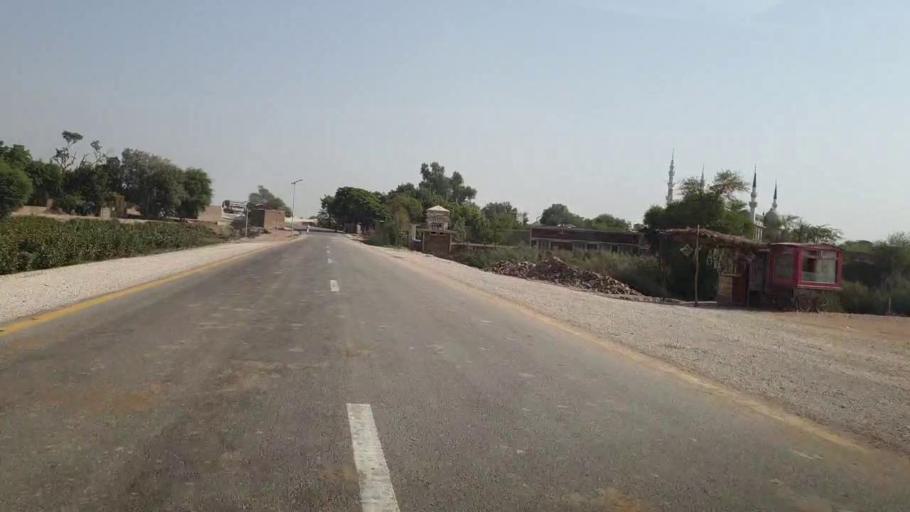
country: PK
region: Sindh
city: Bhan
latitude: 26.5633
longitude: 67.7726
